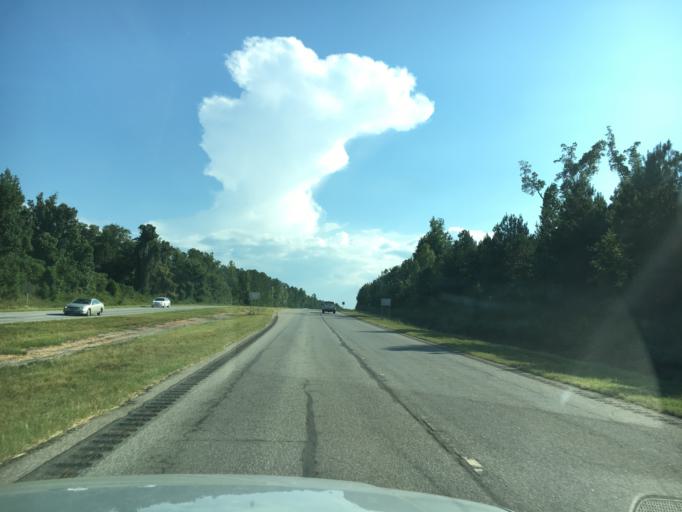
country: US
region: South Carolina
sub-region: Laurens County
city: Clinton
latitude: 34.3901
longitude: -81.9439
